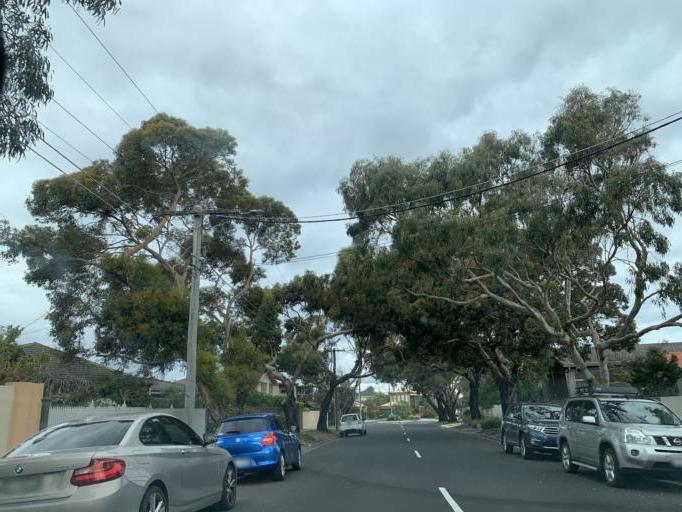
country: AU
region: Victoria
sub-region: Bayside
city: Black Rock
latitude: -37.9794
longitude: 145.0193
